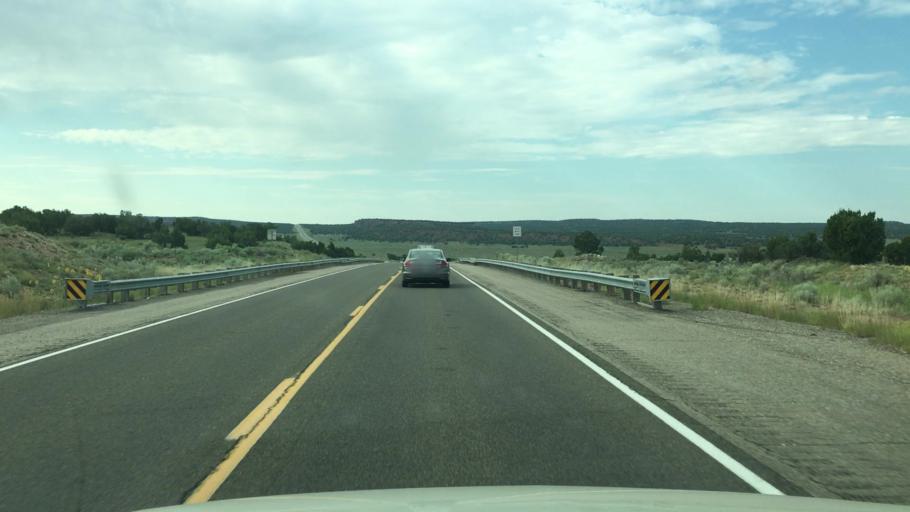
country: US
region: New Mexico
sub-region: Santa Fe County
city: Eldorado at Santa Fe
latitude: 35.2582
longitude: -105.8087
